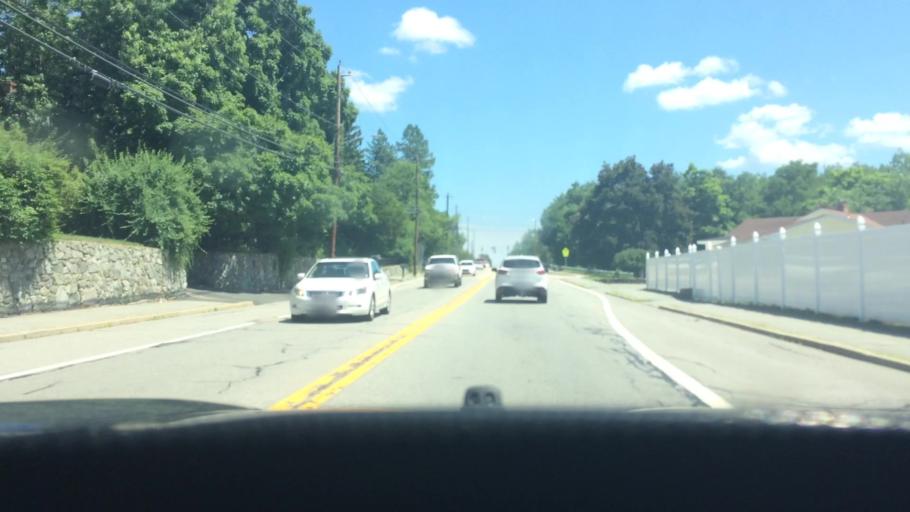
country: US
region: Massachusetts
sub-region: Worcester County
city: Millville
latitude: 42.0052
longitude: -71.5710
